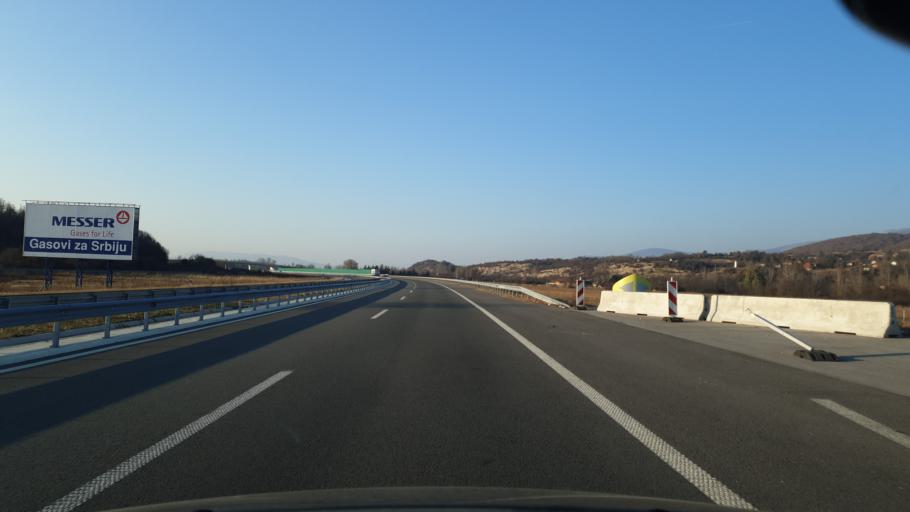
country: RS
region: Central Serbia
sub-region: Pirotski Okrug
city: Dimitrovgrad
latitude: 43.0542
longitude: 22.6974
